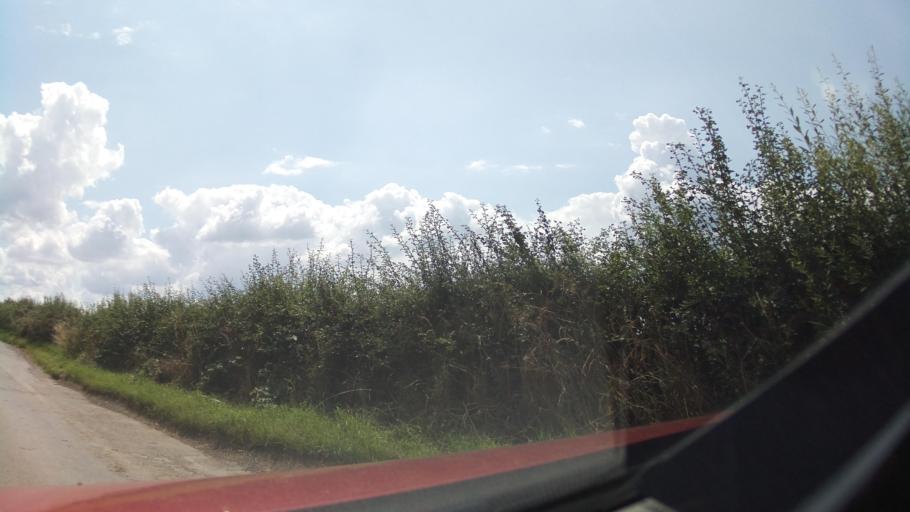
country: GB
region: England
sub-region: Oxfordshire
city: Shrivenham
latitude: 51.5877
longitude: -1.6734
